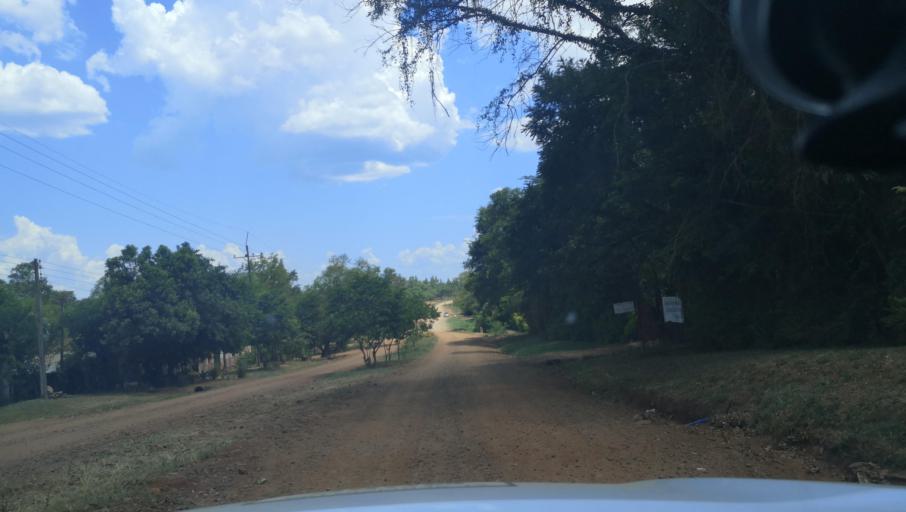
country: PY
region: Itapua
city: Carmen del Parana
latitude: -27.1673
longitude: -56.2490
